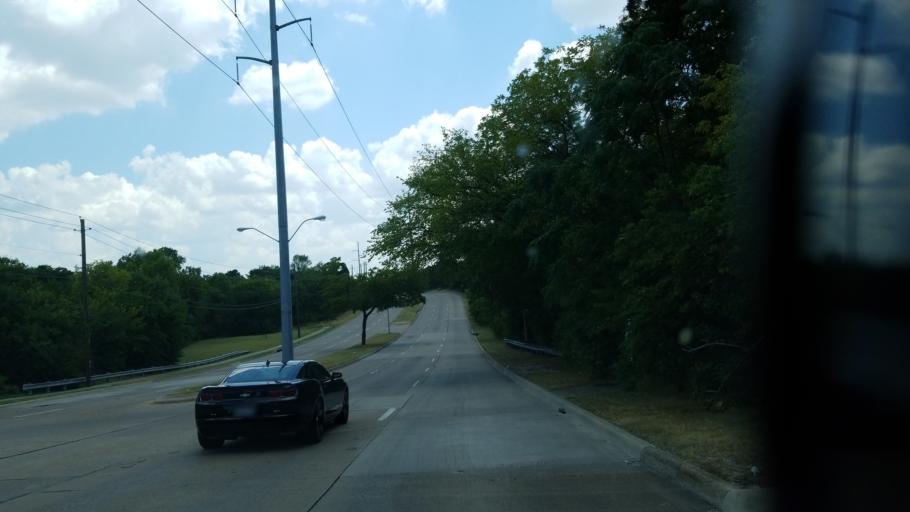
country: US
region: Texas
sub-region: Dallas County
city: Duncanville
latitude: 32.6745
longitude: -96.8829
